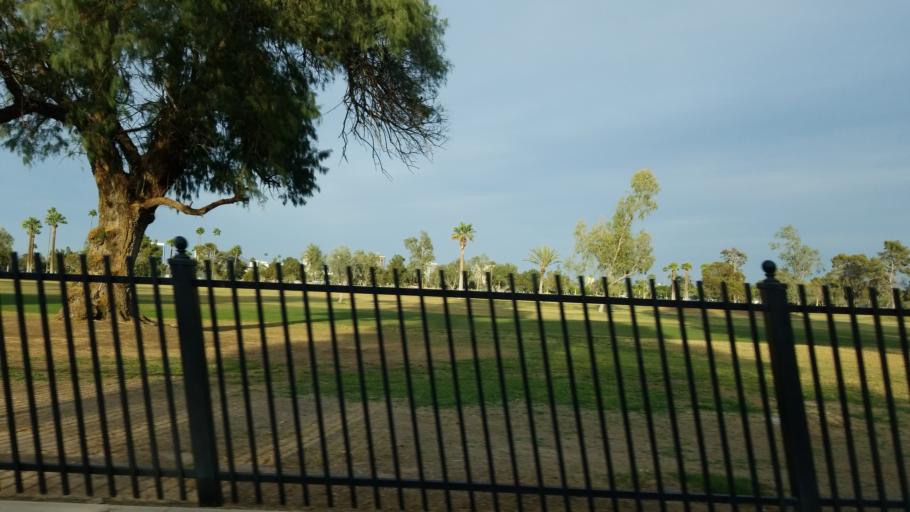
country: US
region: Arizona
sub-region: Maricopa County
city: Phoenix
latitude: 33.4783
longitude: -112.0998
